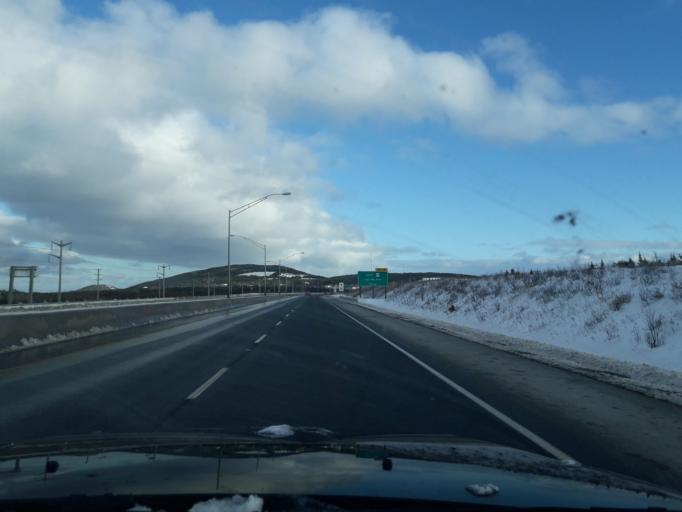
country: CA
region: Newfoundland and Labrador
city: St. John's
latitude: 47.6133
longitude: -52.7013
